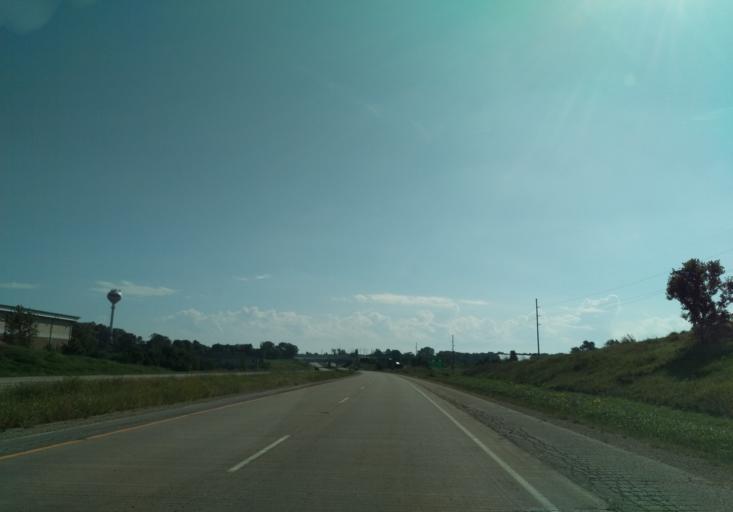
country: US
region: Wisconsin
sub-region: Dane County
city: Verona
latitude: 42.9730
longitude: -89.5325
